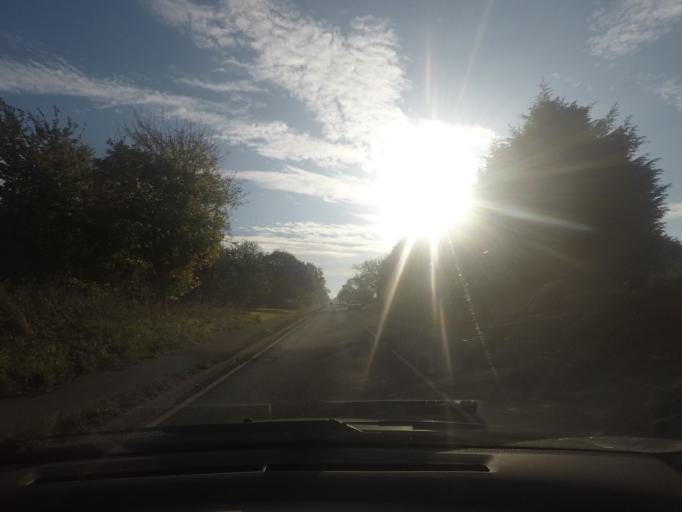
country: GB
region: England
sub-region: East Riding of Yorkshire
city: Market Weighton
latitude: 53.8579
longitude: -0.6545
